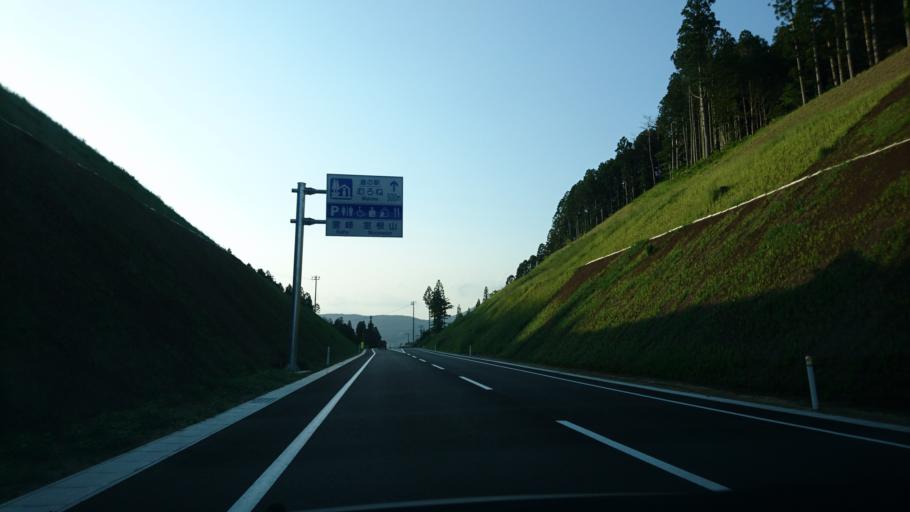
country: JP
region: Iwate
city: Ofunato
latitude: 38.9289
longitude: 141.4530
